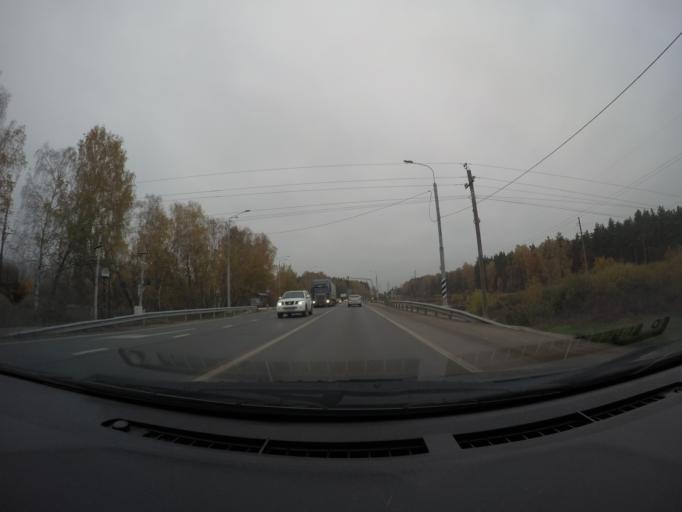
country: RU
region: Moskovskaya
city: Malyshevo
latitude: 55.4797
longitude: 38.3464
